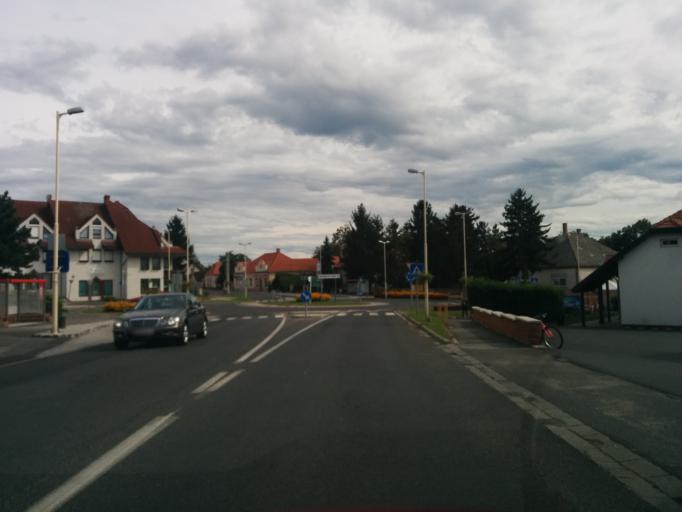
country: HU
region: Vas
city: Buk
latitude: 47.3815
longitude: 16.7563
